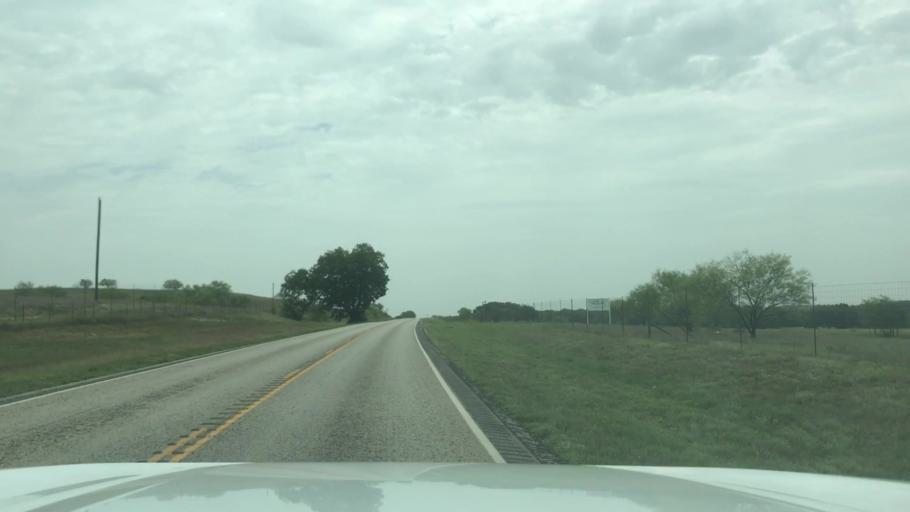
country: US
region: Texas
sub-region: Erath County
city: Dublin
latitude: 32.0571
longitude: -98.1861
